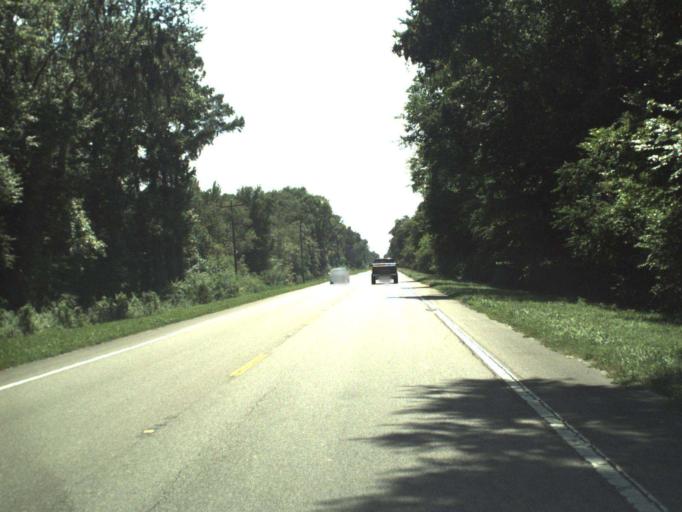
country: US
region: Florida
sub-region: Lake County
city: Mascotte
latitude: 28.5723
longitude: -81.9998
